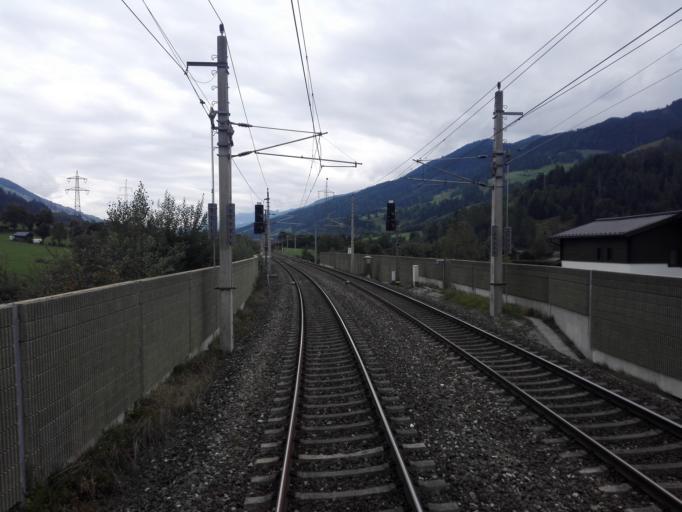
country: AT
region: Salzburg
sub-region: Politischer Bezirk Zell am See
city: Bruck an der Grossglocknerstrasse
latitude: 47.2836
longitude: 12.8378
